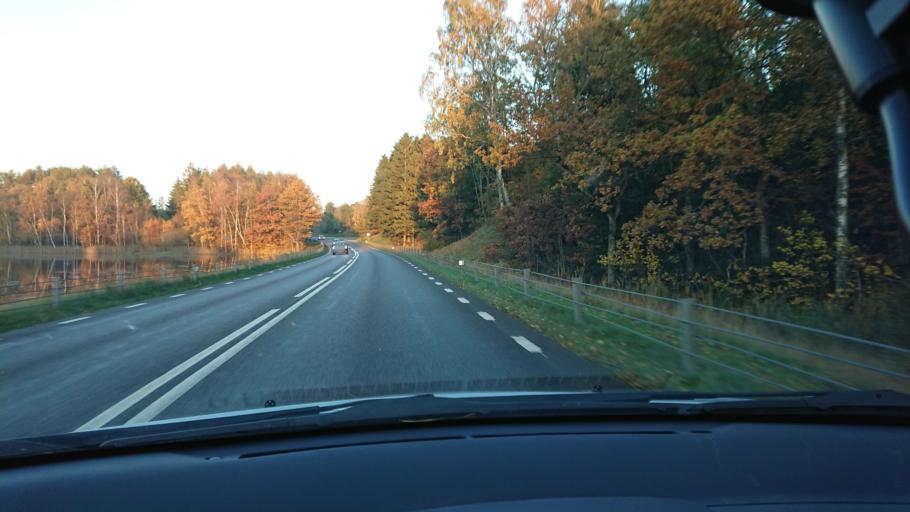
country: SE
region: Halland
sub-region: Halmstads Kommun
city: Aled
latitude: 56.7055
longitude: 13.0273
